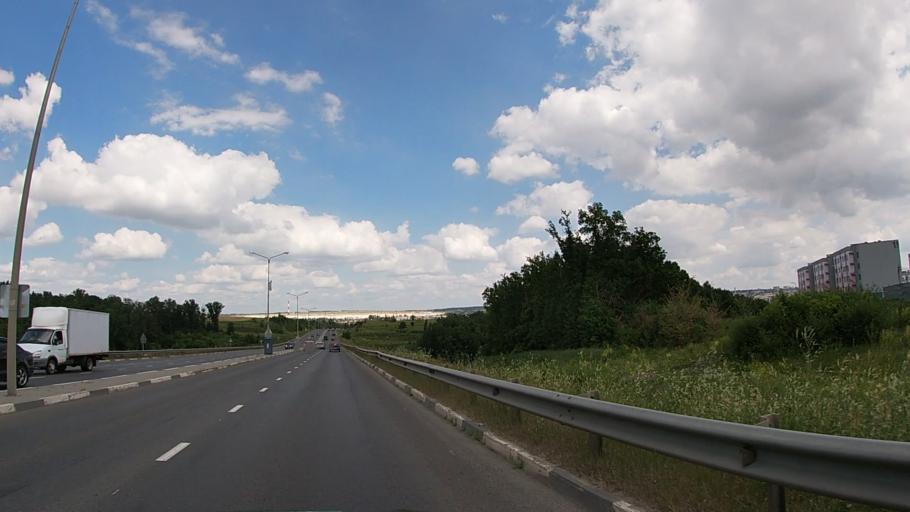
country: RU
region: Belgorod
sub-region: Belgorodskiy Rayon
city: Belgorod
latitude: 50.5985
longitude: 36.5303
